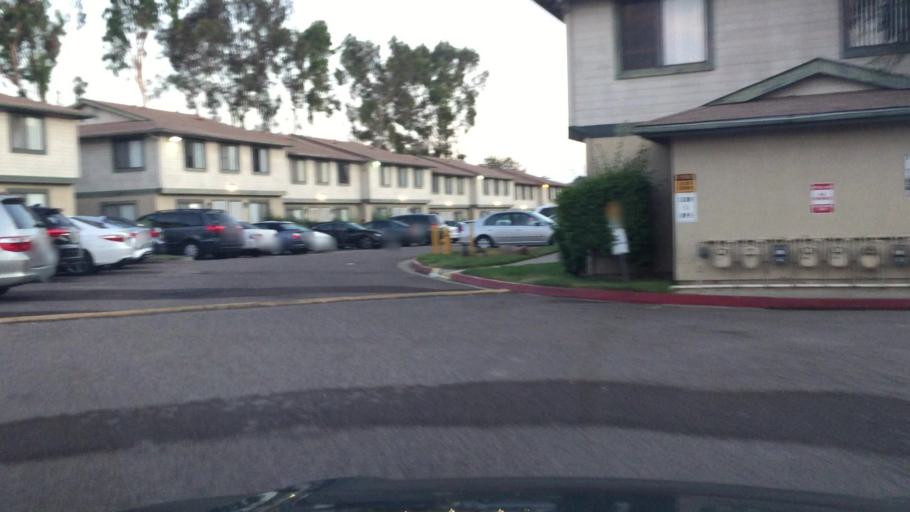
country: US
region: California
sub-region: San Diego County
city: Bostonia
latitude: 32.8203
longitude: -116.9554
